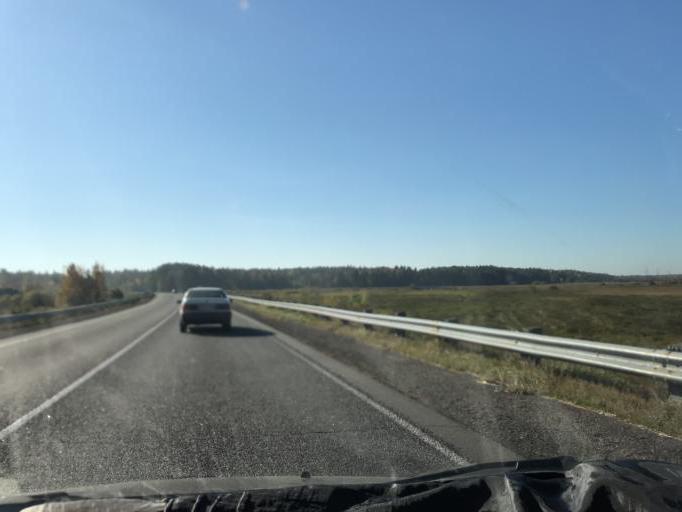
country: BY
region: Mogilev
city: Babruysk
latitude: 53.1766
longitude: 29.0452
